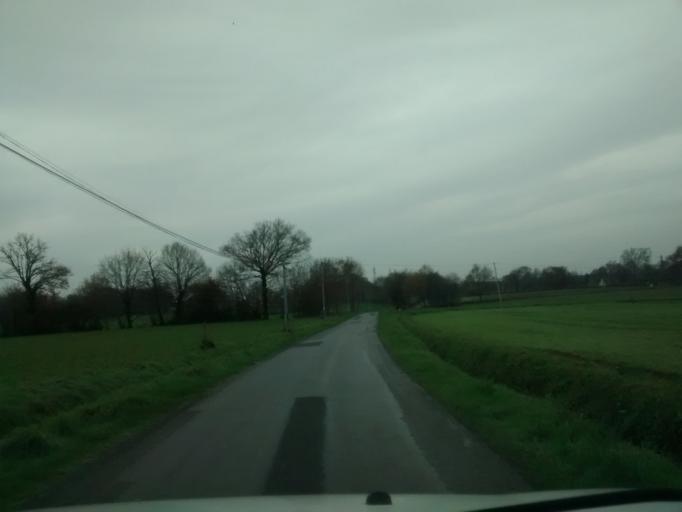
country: FR
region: Brittany
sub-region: Departement d'Ille-et-Vilaine
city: Fouillard
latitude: 48.1454
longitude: -1.5589
